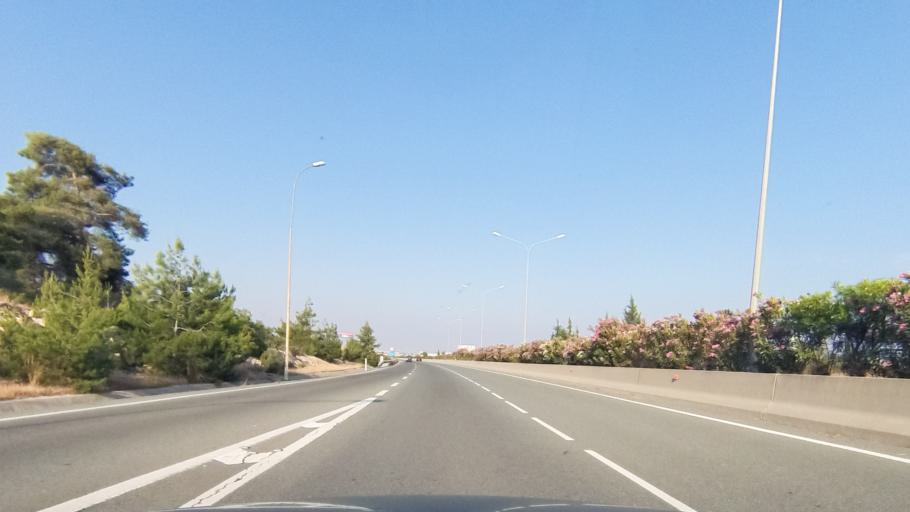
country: CY
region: Limassol
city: Erimi
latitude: 34.6811
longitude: 32.8896
